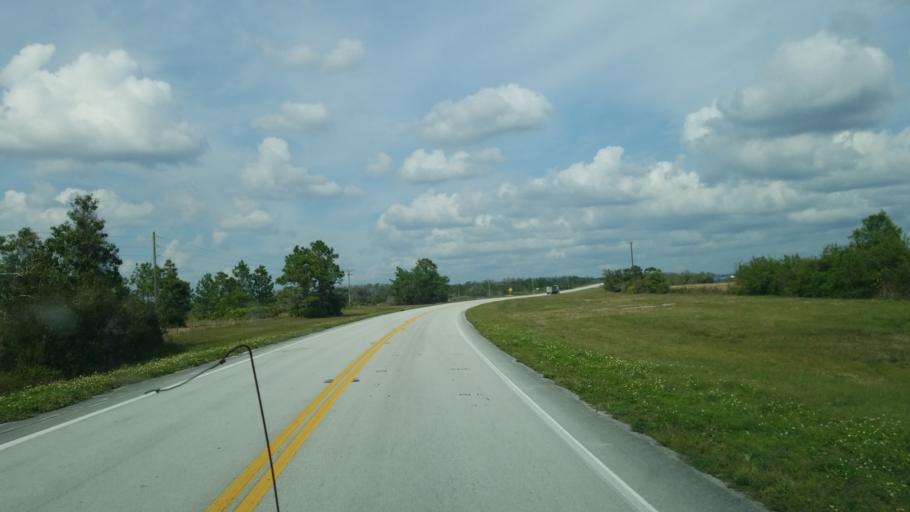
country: US
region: Florida
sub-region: Indian River County
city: Fellsmere
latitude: 27.7217
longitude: -80.9148
